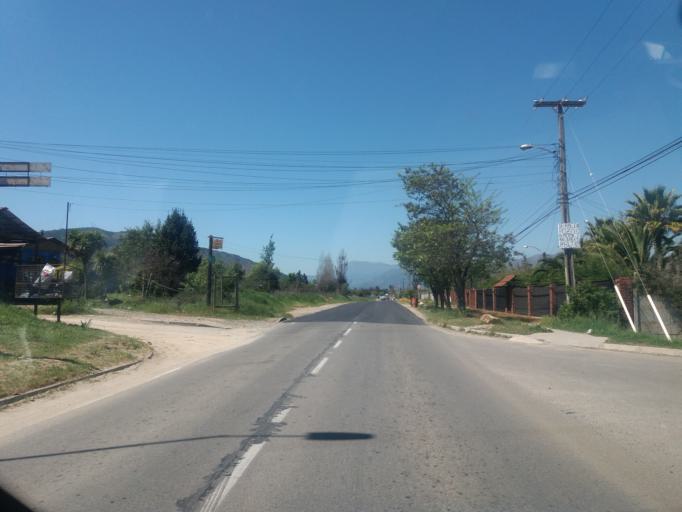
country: CL
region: Valparaiso
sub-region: Provincia de Marga Marga
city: Limache
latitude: -32.9718
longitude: -71.3002
